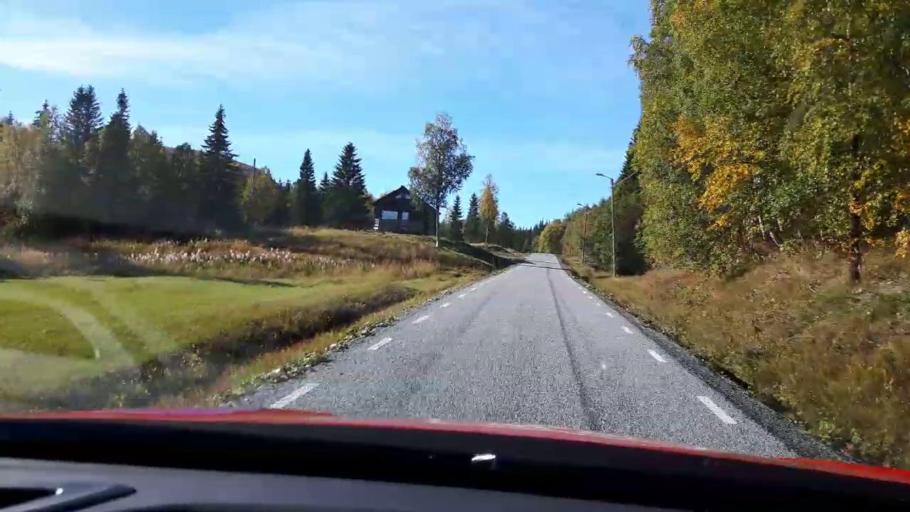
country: NO
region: Nord-Trondelag
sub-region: Royrvik
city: Royrvik
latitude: 64.7290
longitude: 13.9472
